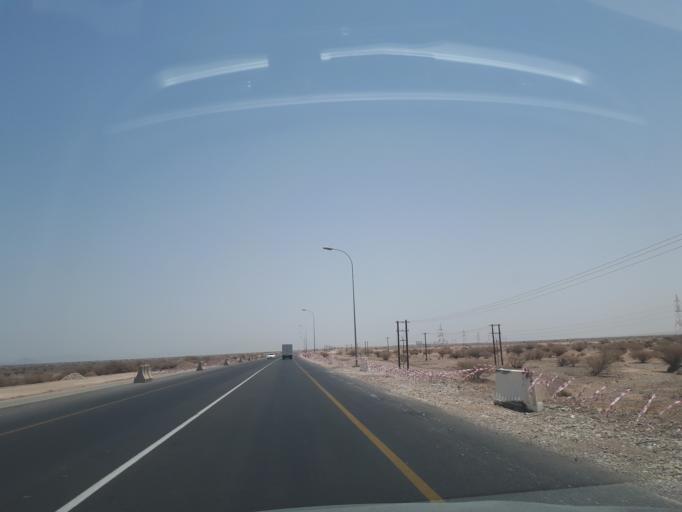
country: OM
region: Ash Sharqiyah
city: Badiyah
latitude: 22.4179
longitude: 59.0495
